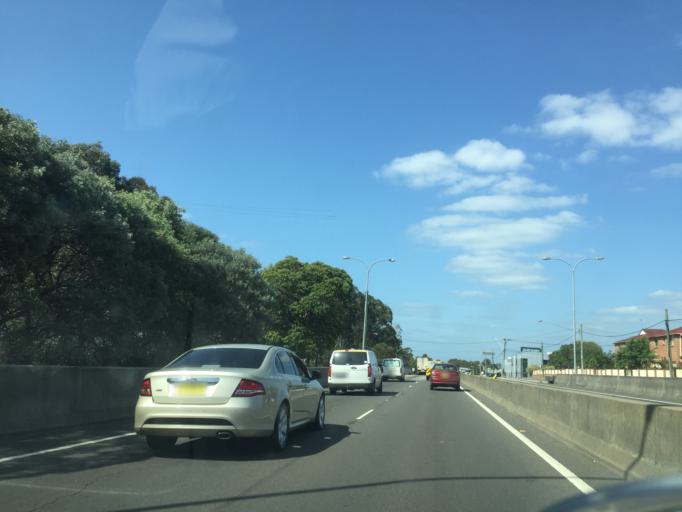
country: AU
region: New South Wales
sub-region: Strathfield
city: Strathfield South
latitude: -33.8886
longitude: 151.0675
